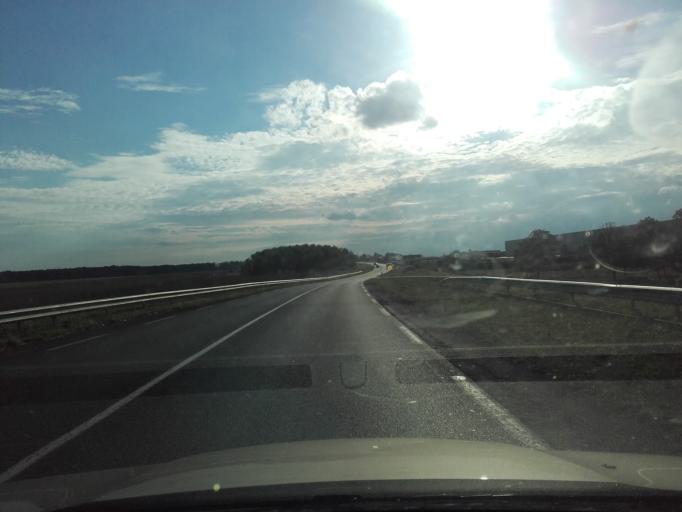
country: FR
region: Centre
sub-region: Departement d'Indre-et-Loire
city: Parcay-Meslay
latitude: 47.4739
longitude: 0.7572
